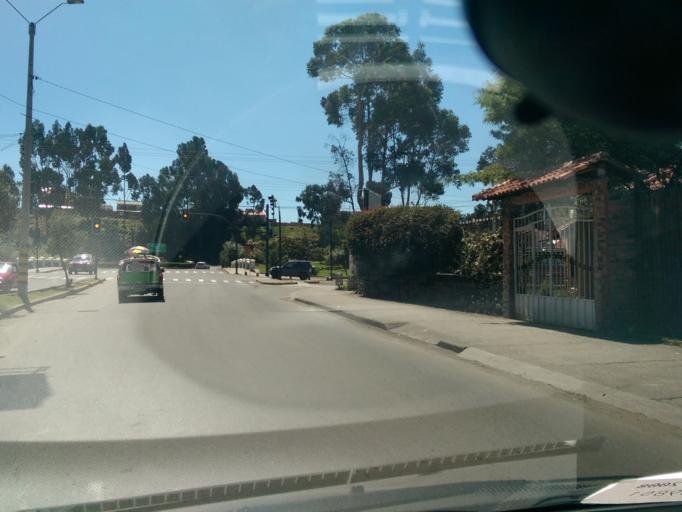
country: EC
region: Azuay
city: Cuenca
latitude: -2.9100
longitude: -79.0194
